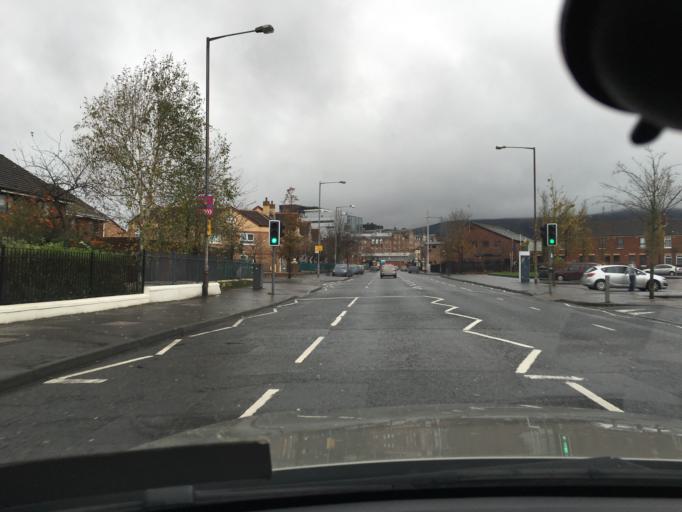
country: GB
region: Northern Ireland
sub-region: City of Belfast
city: Belfast
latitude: 54.5952
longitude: -5.9478
